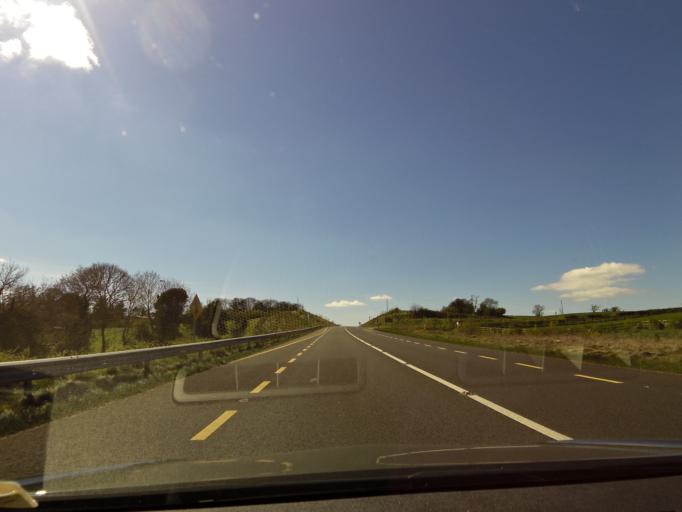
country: IE
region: Leinster
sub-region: Kildare
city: Moone
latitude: 53.0001
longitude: -6.8231
